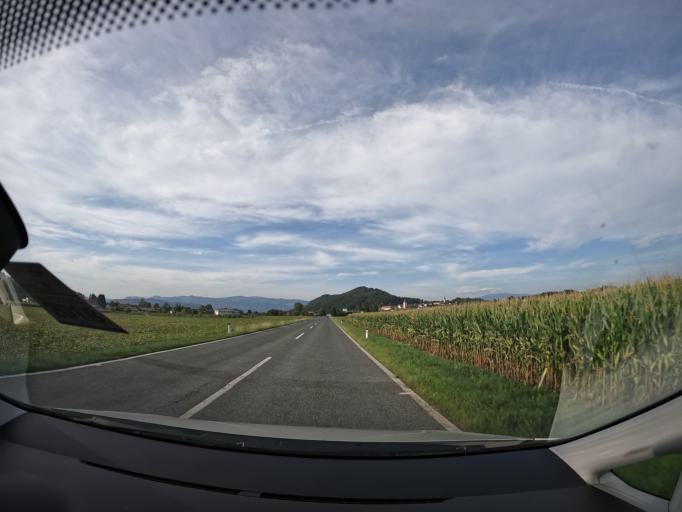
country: AT
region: Carinthia
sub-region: Politischer Bezirk Volkermarkt
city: Eberndorf
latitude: 46.5846
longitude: 14.6294
